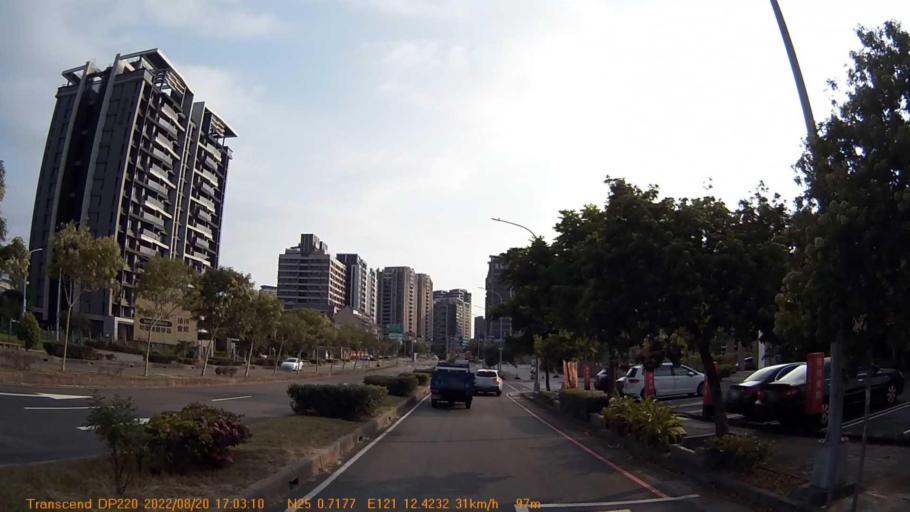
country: TW
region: Taiwan
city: Taoyuan City
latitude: 25.0117
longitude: 121.2068
